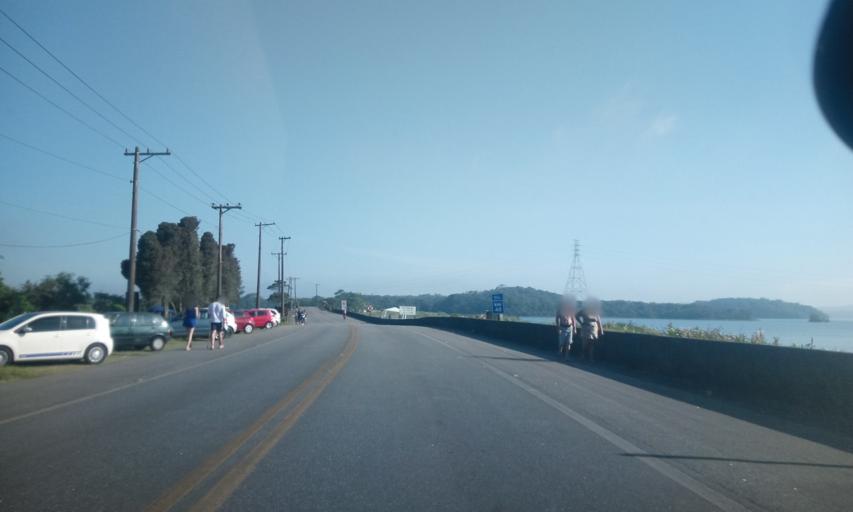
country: BR
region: Sao Paulo
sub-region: Cubatao
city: Cubatao
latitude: -23.8383
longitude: -46.4723
